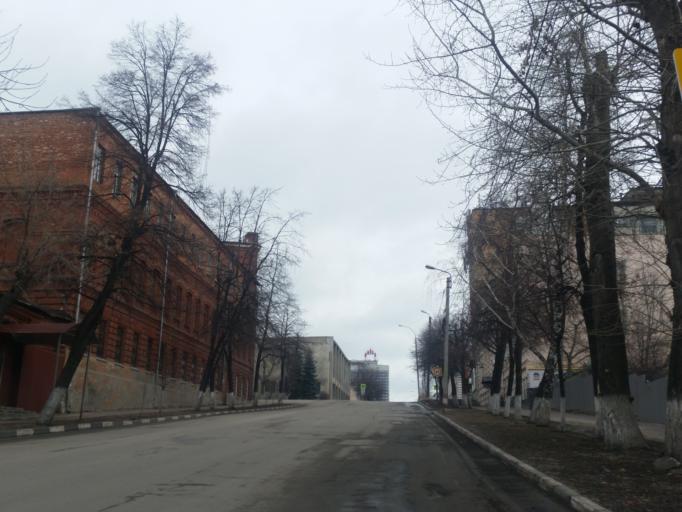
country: RU
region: Ulyanovsk
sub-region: Ulyanovskiy Rayon
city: Ulyanovsk
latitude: 54.3130
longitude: 48.3995
